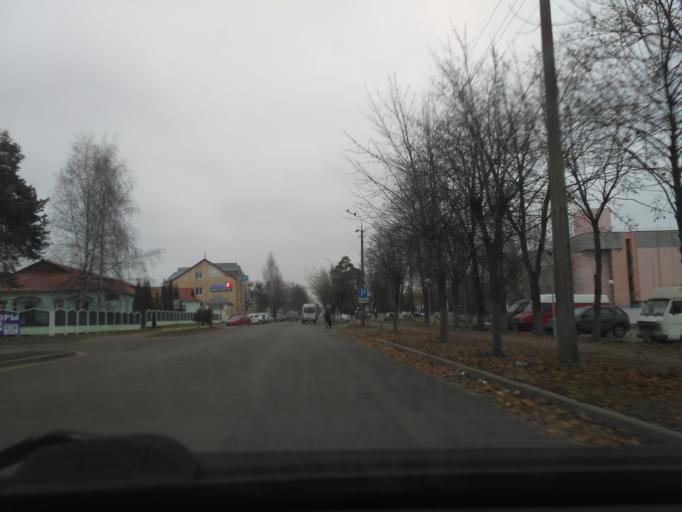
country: BY
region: Minsk
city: Horad Barysaw
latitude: 54.2085
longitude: 28.4889
